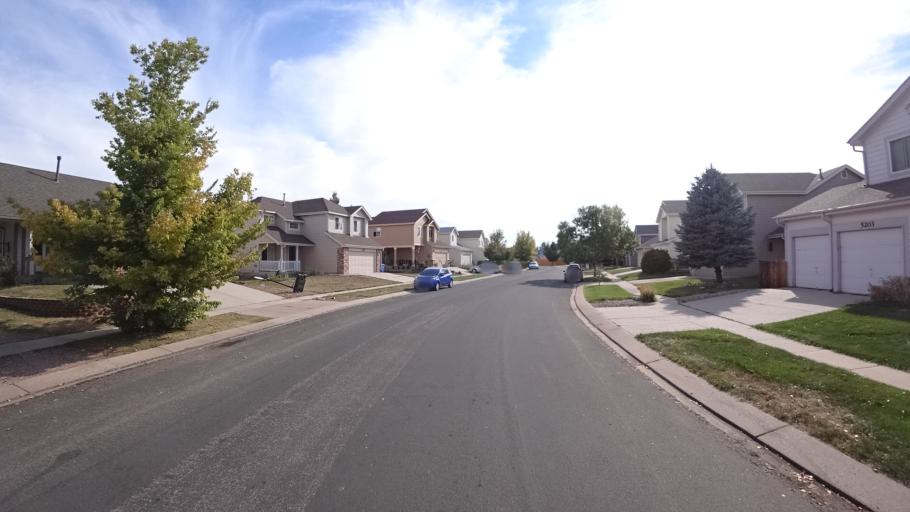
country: US
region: Colorado
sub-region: El Paso County
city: Cimarron Hills
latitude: 38.9065
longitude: -104.6949
